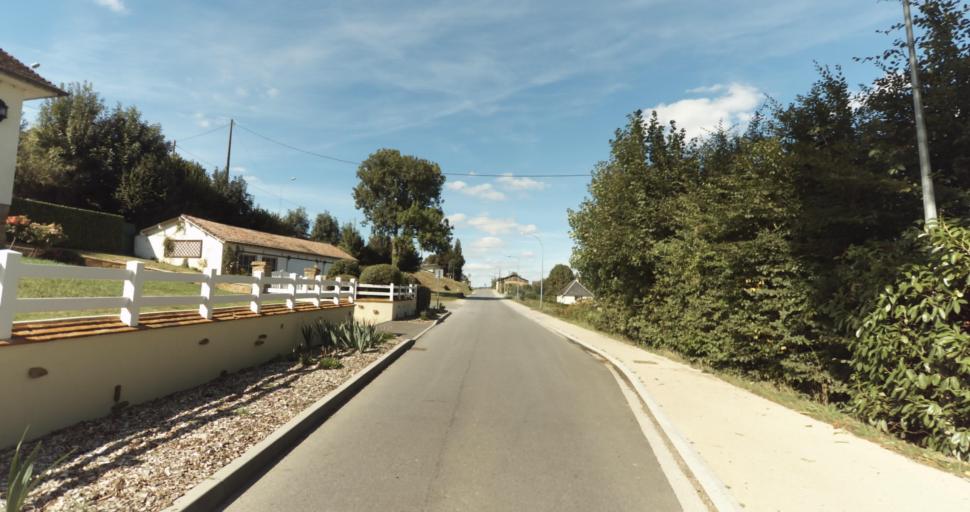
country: FR
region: Lower Normandy
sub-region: Departement de l'Orne
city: Vimoutiers
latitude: 48.9188
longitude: 0.2004
